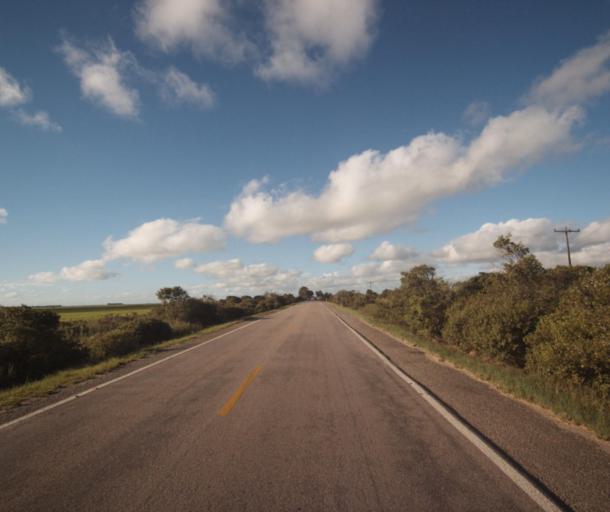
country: BR
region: Rio Grande do Sul
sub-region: Arroio Grande
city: Arroio Grande
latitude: -32.4880
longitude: -52.5797
